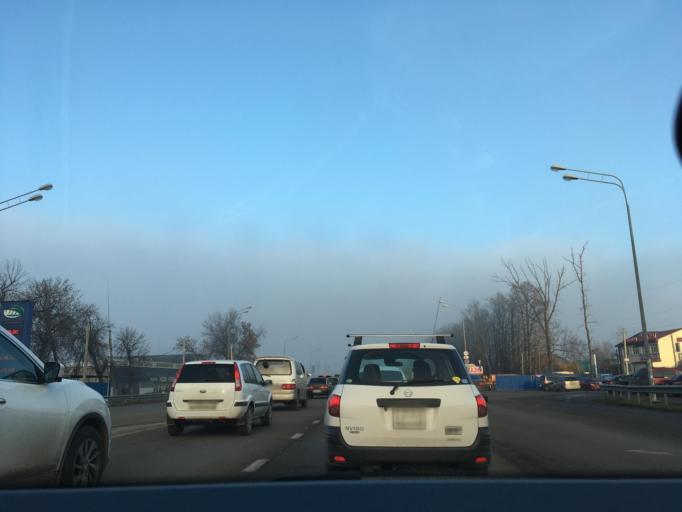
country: RU
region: Krasnodarskiy
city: Krasnodar
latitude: 45.1332
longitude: 39.0244
